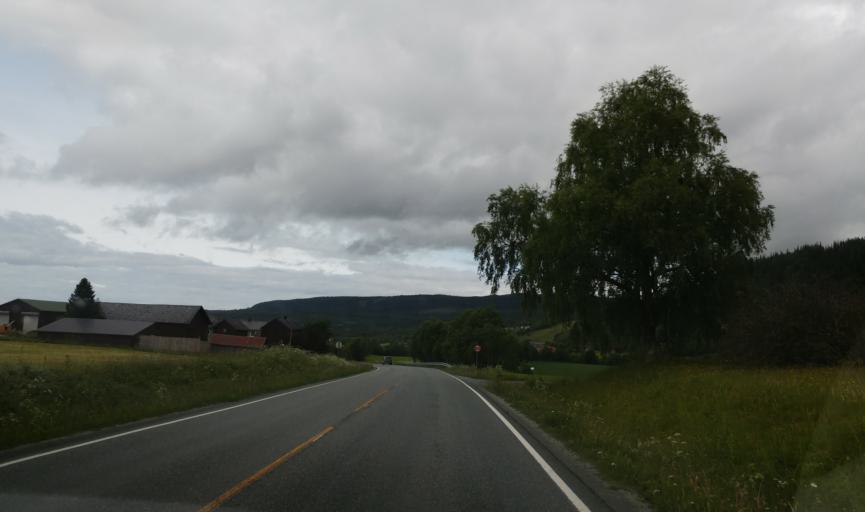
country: NO
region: Sor-Trondelag
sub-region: Selbu
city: Mebonden
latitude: 63.3837
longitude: 11.0811
